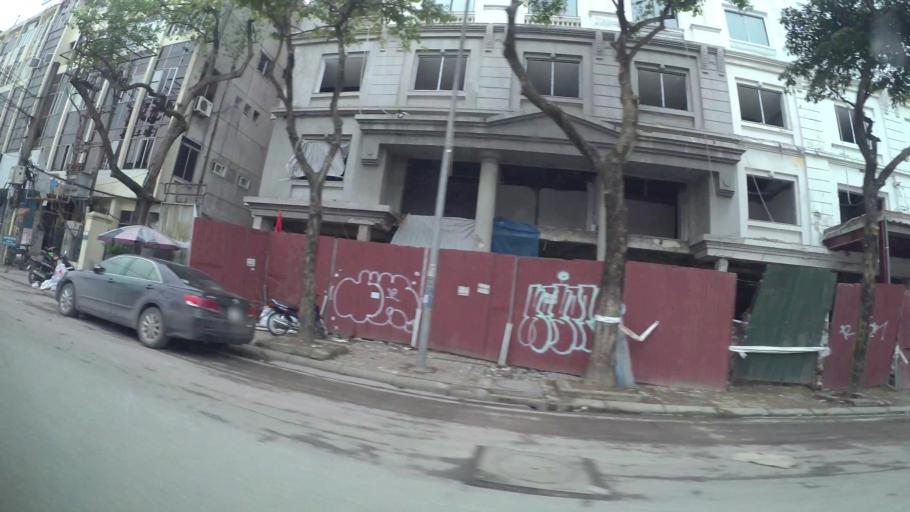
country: VN
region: Ha Noi
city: Hoan Kiem
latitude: 21.0225
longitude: 105.8610
